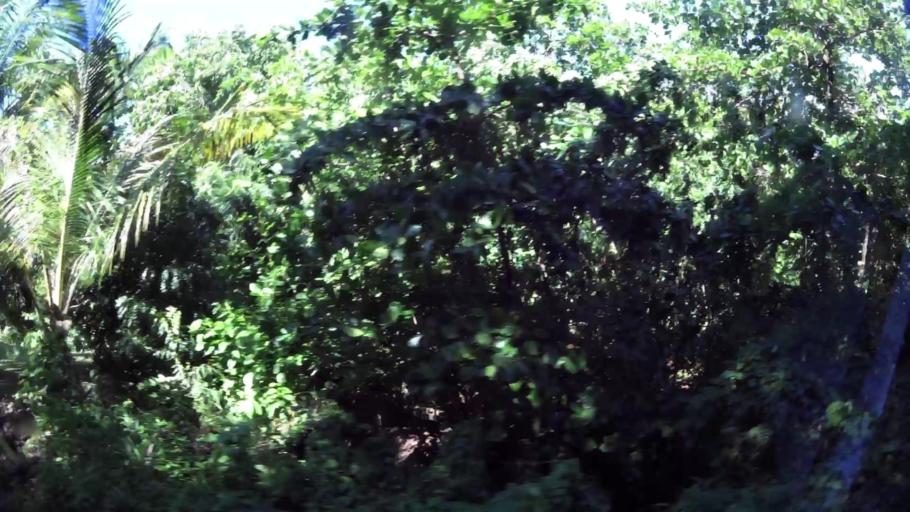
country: MS
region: Saint Peter
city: Saint Peters
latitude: 16.7414
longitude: -62.2182
